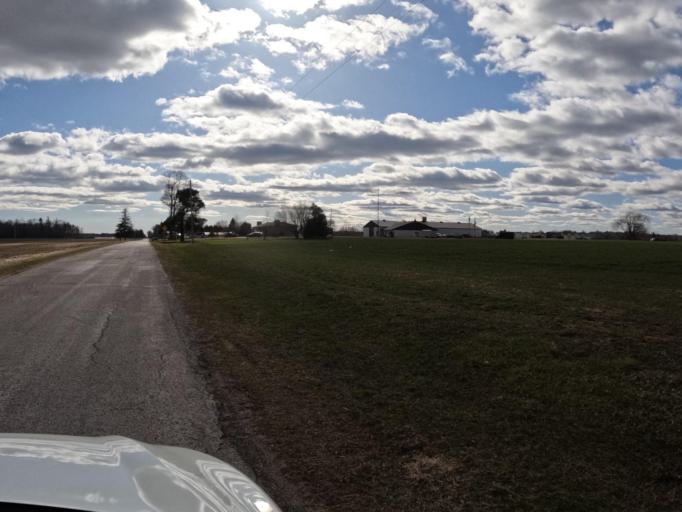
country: CA
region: Ontario
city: Norfolk County
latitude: 42.7519
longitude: -80.3833
